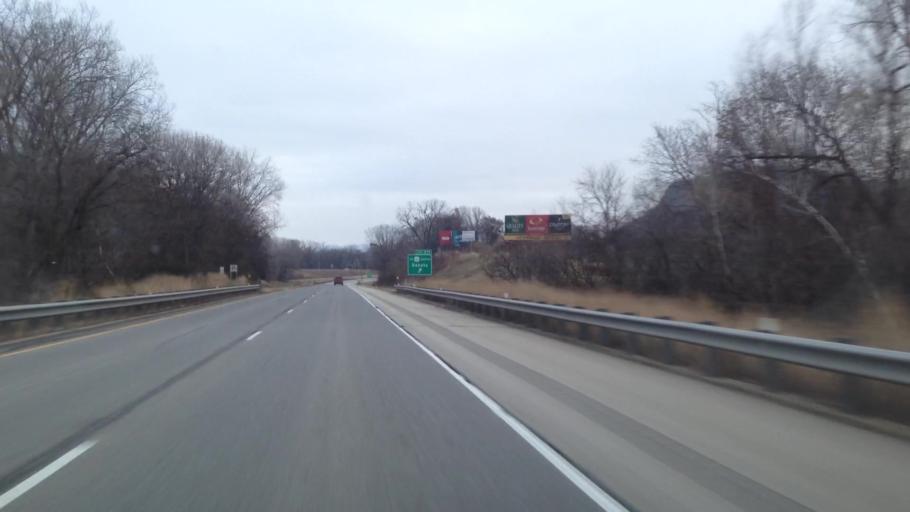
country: US
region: Wisconsin
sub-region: La Crosse County
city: Brice Prairie
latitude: 43.9165
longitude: -91.3698
